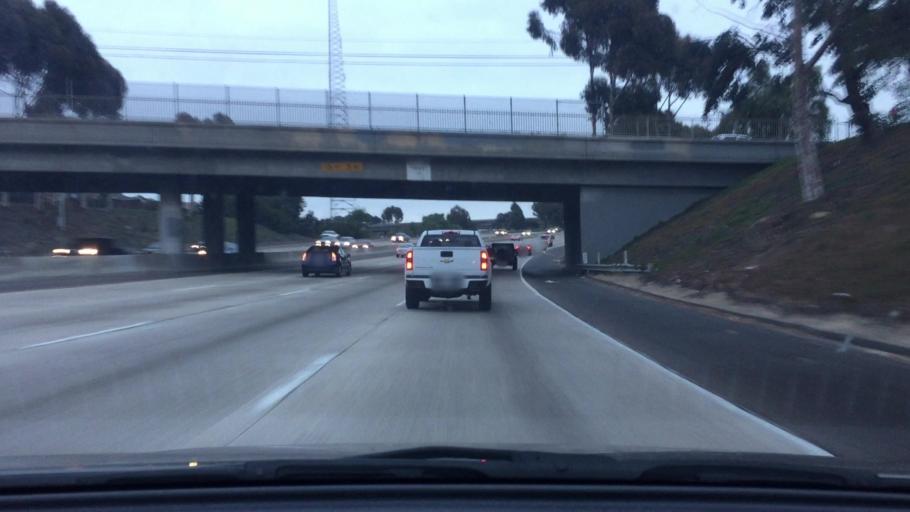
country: US
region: California
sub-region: San Diego County
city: National City
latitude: 32.6943
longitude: -117.1258
